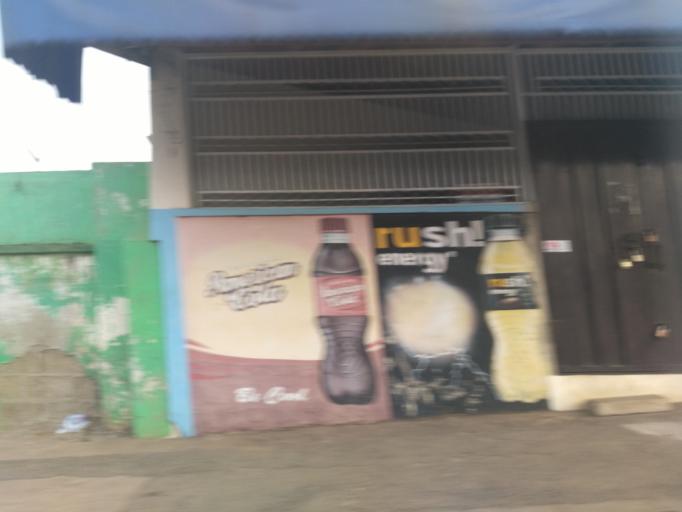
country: GH
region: Ashanti
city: Kumasi
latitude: 6.6866
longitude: -1.6214
